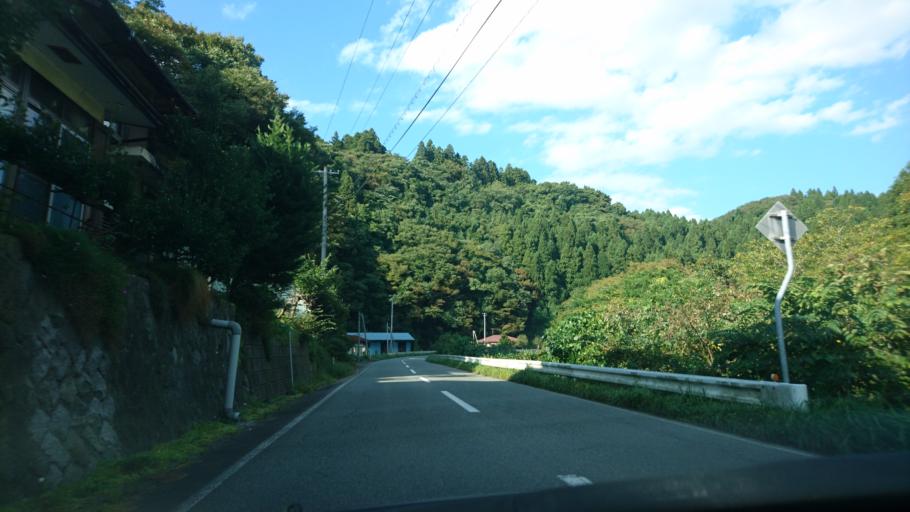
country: JP
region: Iwate
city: Ichinoseki
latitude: 38.8578
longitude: 141.3143
